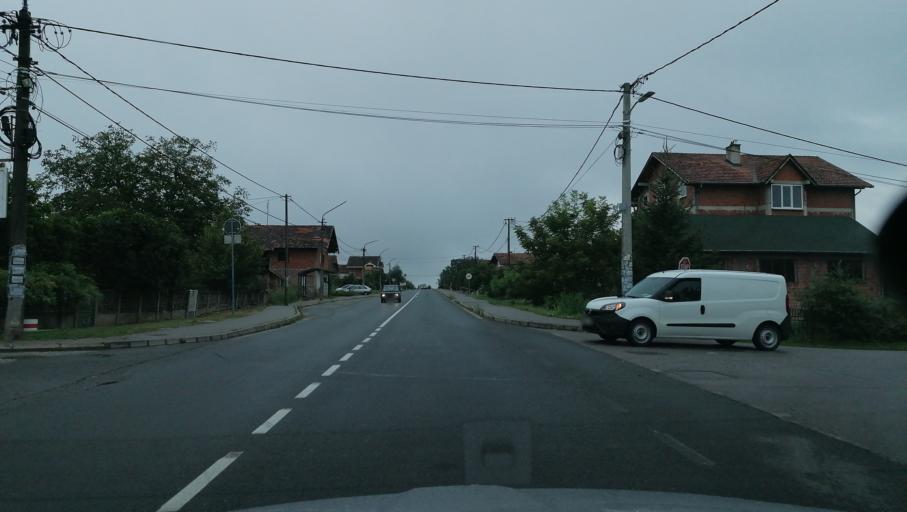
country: RS
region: Central Serbia
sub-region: Rasinski Okrug
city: Krusevac
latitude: 43.5878
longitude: 21.2696
